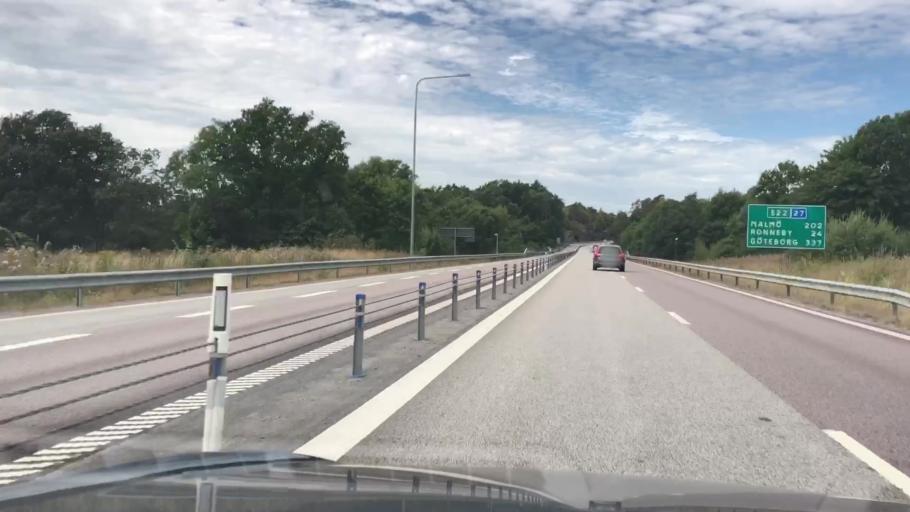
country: SE
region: Blekinge
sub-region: Karlskrona Kommun
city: Rodeby
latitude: 56.2063
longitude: 15.6363
